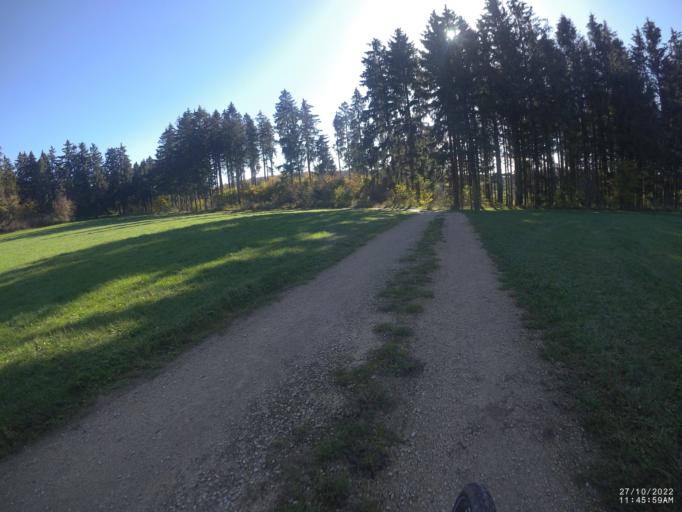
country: DE
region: Baden-Wuerttemberg
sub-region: Regierungsbezirk Stuttgart
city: Bad Ditzenbach
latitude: 48.5476
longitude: 9.7179
